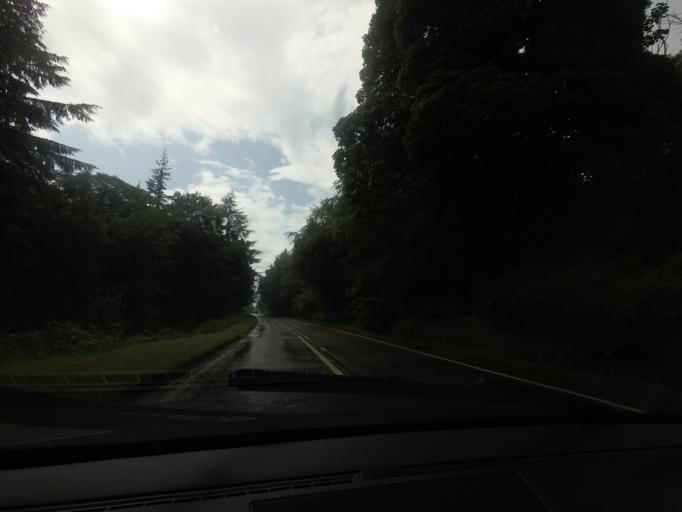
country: GB
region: Scotland
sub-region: Moray
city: Fochabers
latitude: 57.6131
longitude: -3.0764
